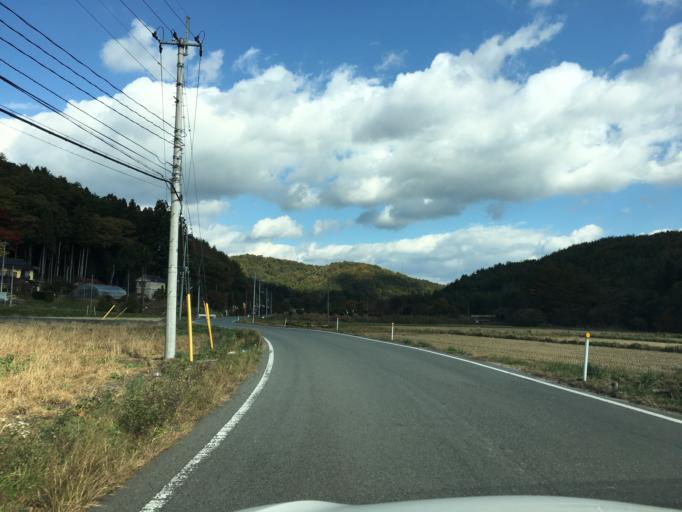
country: JP
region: Fukushima
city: Funehikimachi-funehiki
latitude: 37.3304
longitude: 140.7920
